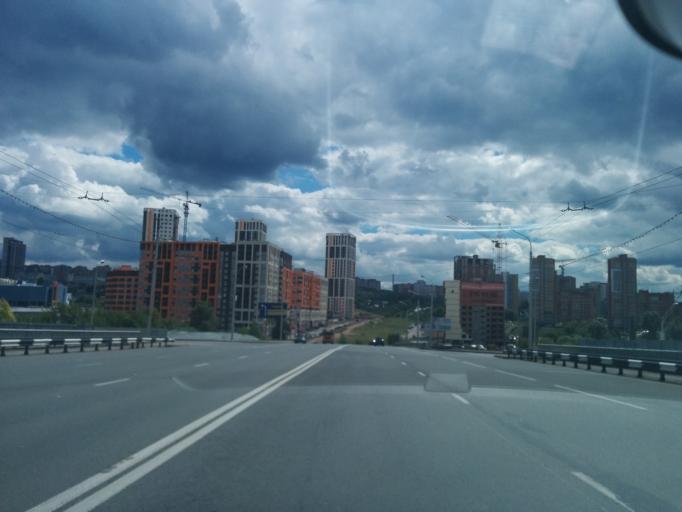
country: RU
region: Bashkortostan
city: Ufa
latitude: 54.7208
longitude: 55.9773
